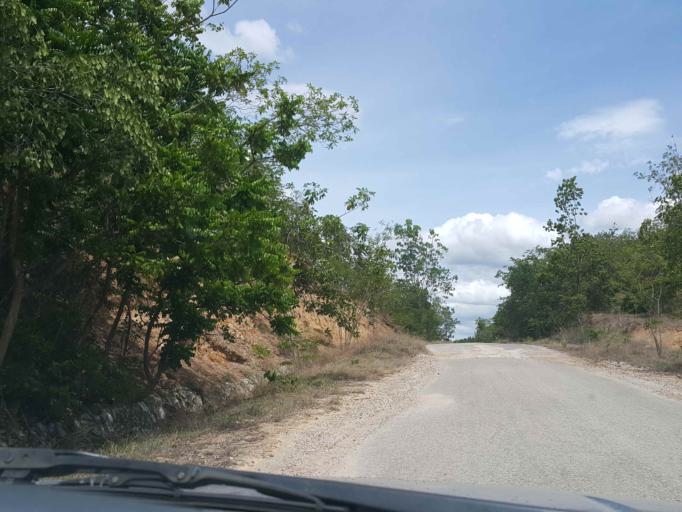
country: TH
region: Chiang Mai
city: Doi Lo
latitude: 18.5274
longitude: 98.7506
